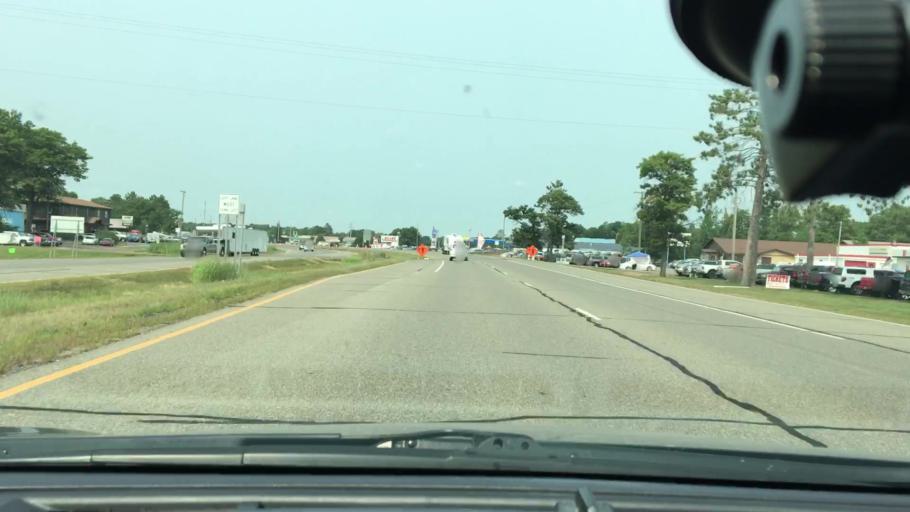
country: US
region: Minnesota
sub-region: Crow Wing County
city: Baxter
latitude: 46.4134
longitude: -94.2856
